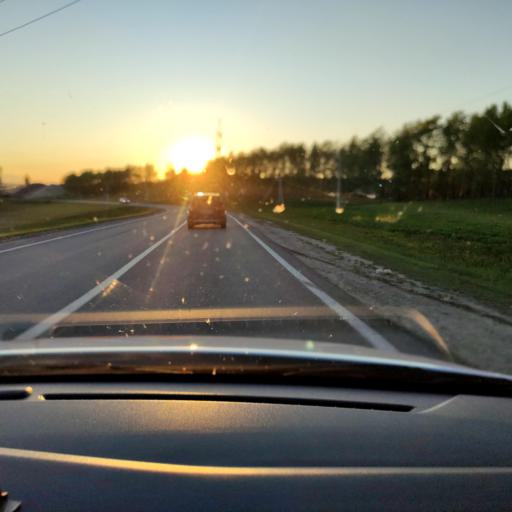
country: RU
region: Tatarstan
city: Pestretsy
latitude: 55.8210
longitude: 49.5334
